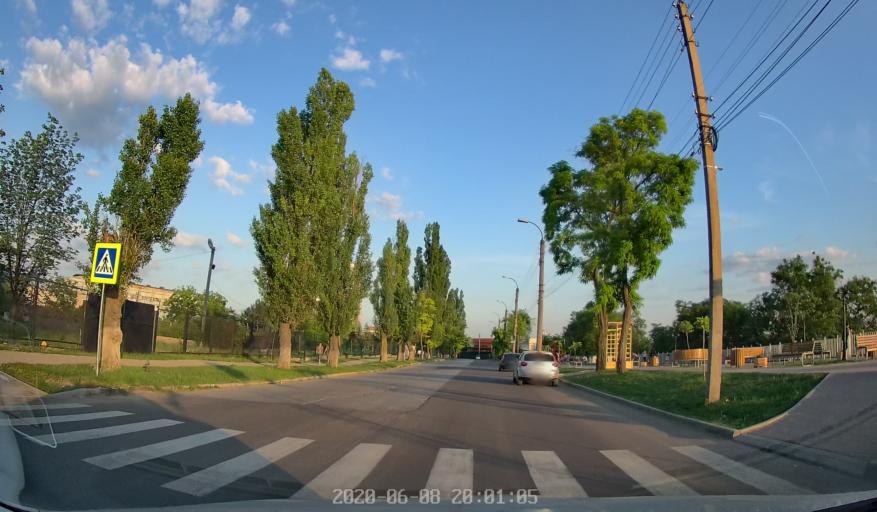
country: MD
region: Chisinau
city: Chisinau
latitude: 47.0140
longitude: 28.8831
